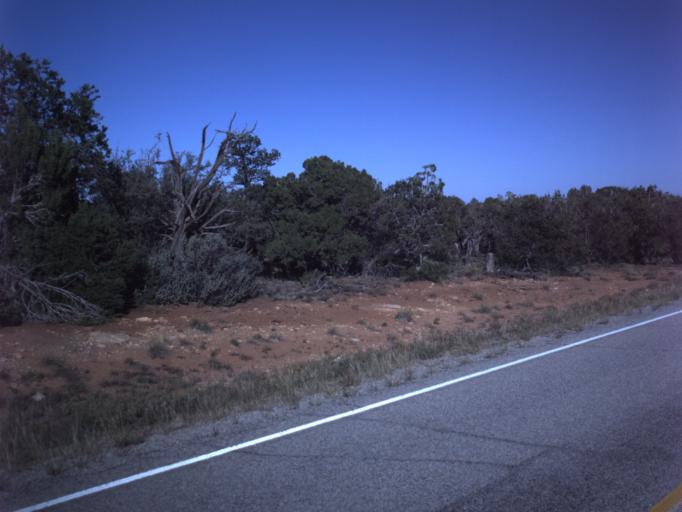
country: US
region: Utah
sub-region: San Juan County
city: Blanding
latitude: 37.5597
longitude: -109.7953
